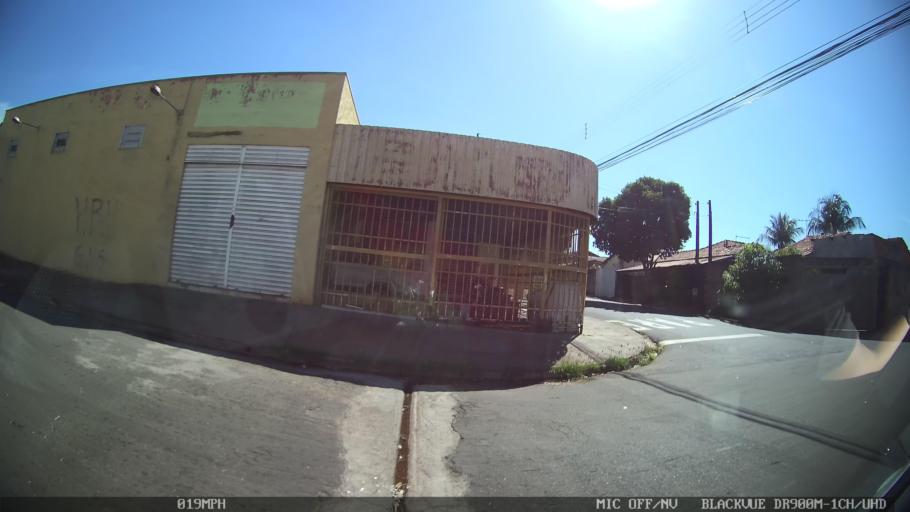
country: BR
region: Sao Paulo
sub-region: Sao Jose Do Rio Preto
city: Sao Jose do Rio Preto
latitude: -20.7706
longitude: -49.4104
